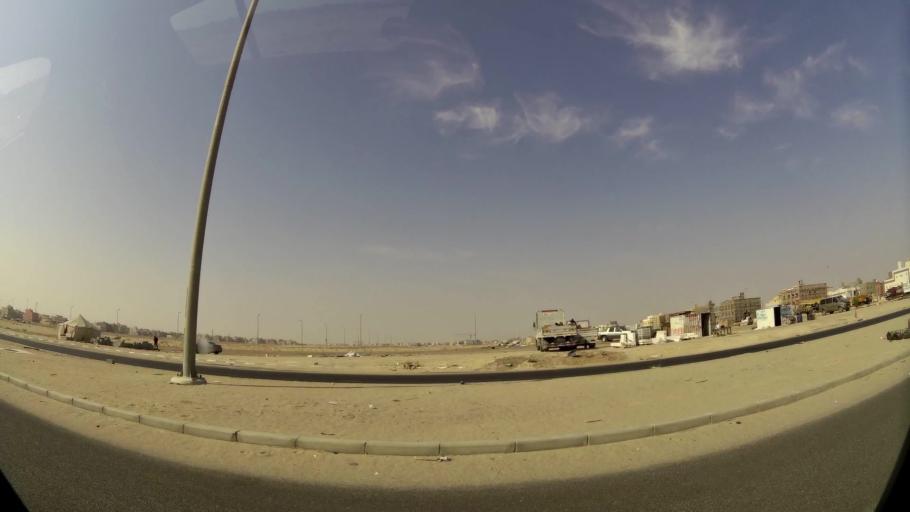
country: KW
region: Al Ahmadi
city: Al Wafrah
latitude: 28.7863
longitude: 48.0689
